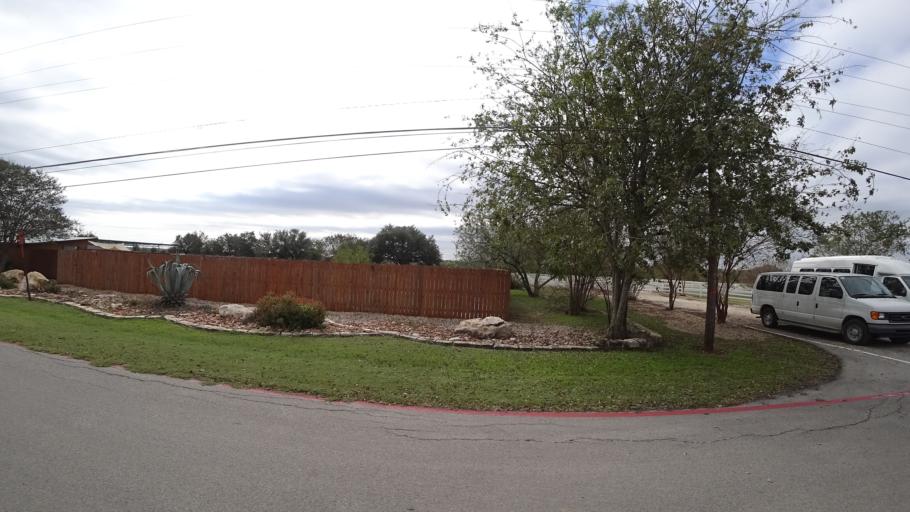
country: US
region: Texas
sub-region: Travis County
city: Manchaca
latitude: 30.1374
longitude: -97.8560
